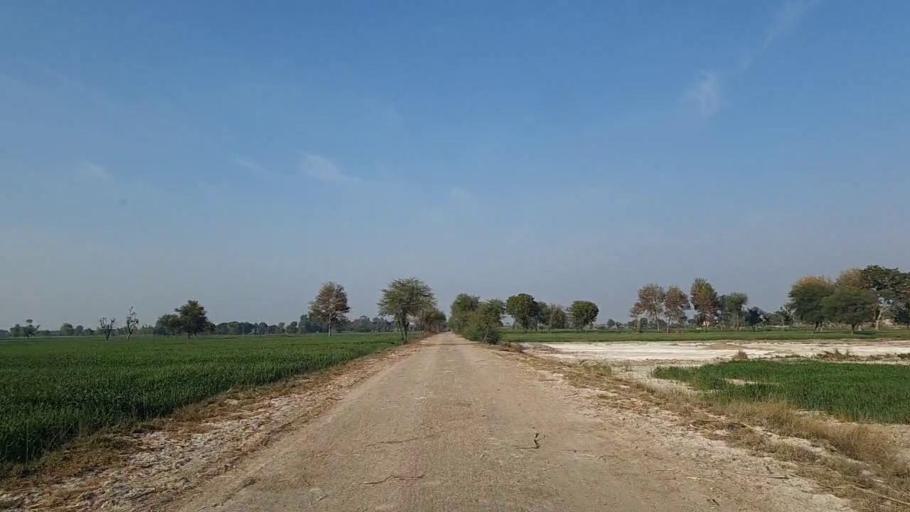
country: PK
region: Sindh
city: Nawabshah
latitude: 26.3760
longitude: 68.4850
